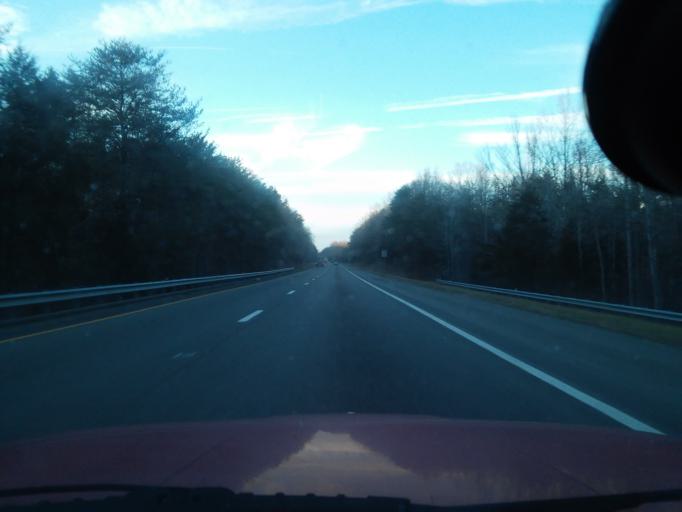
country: US
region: Virginia
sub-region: Louisa County
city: Louisa
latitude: 37.8519
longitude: -77.9900
